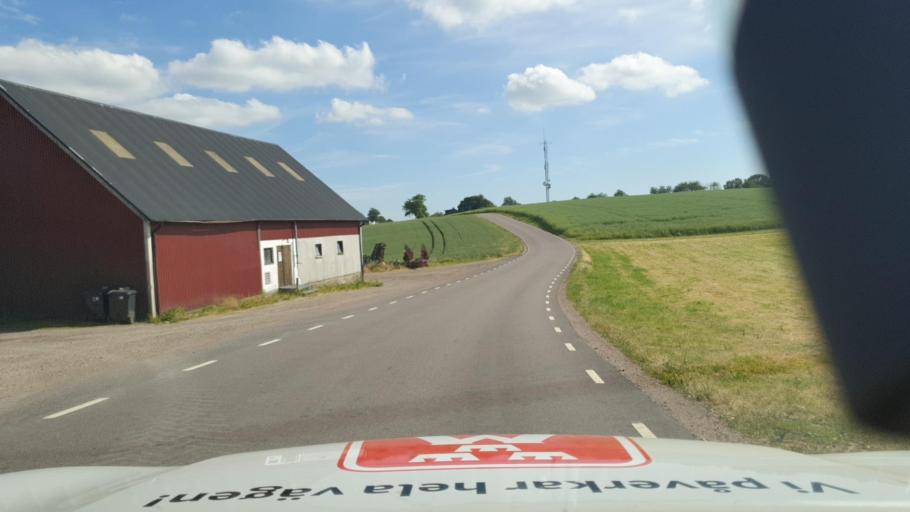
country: SE
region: Skane
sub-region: Sjobo Kommun
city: Blentarp
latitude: 55.5503
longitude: 13.5593
